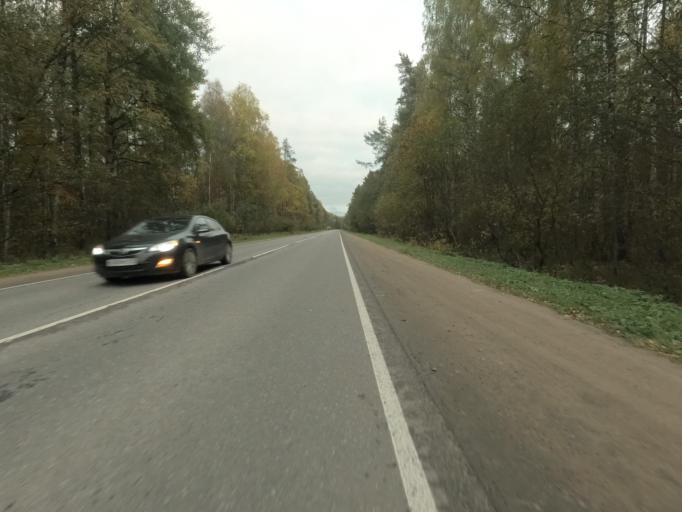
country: RU
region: Leningrad
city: Pavlovo
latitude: 59.8084
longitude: 30.9292
